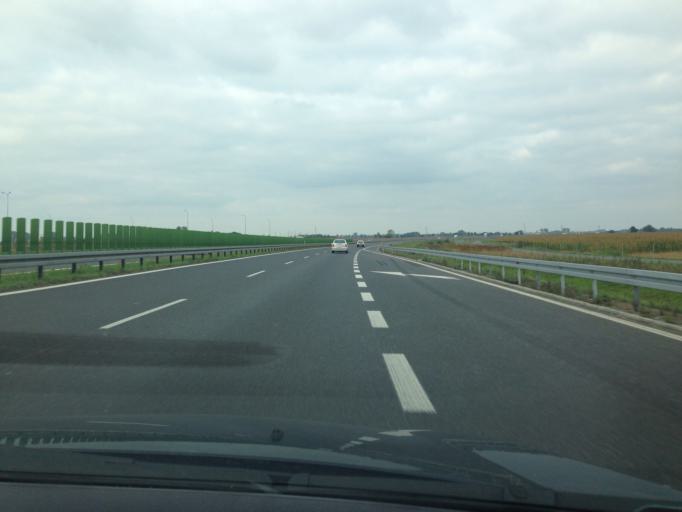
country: PL
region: Greater Poland Voivodeship
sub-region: Powiat poznanski
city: Kostrzyn
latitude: 52.3680
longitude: 17.2043
